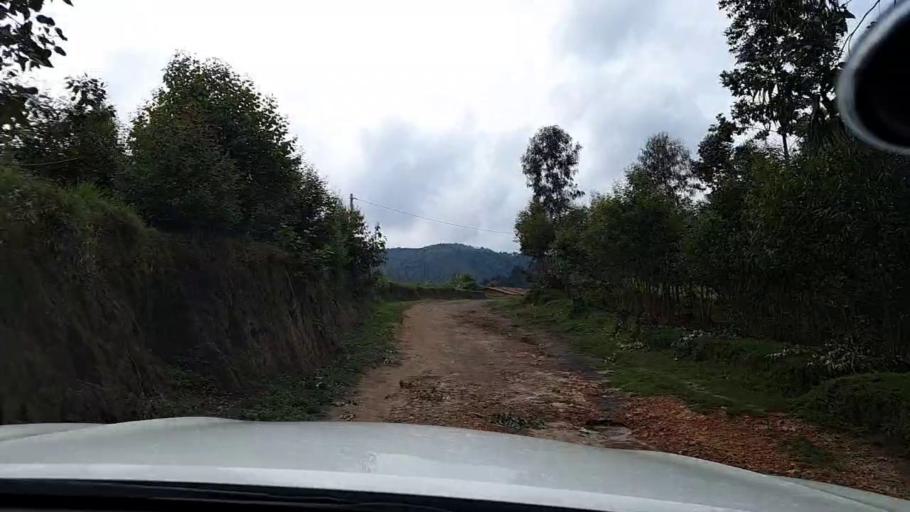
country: RW
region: Western Province
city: Kibuye
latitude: -2.1941
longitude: 29.3181
